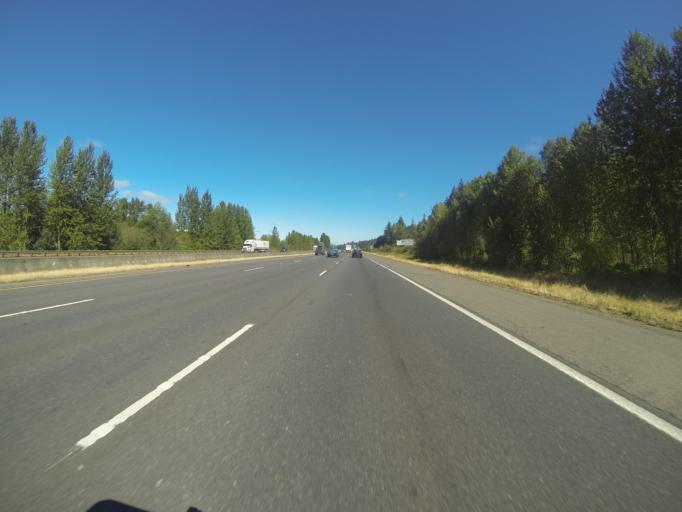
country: US
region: Oregon
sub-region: Columbia County
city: Rainier
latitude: 46.0928
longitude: -122.8713
